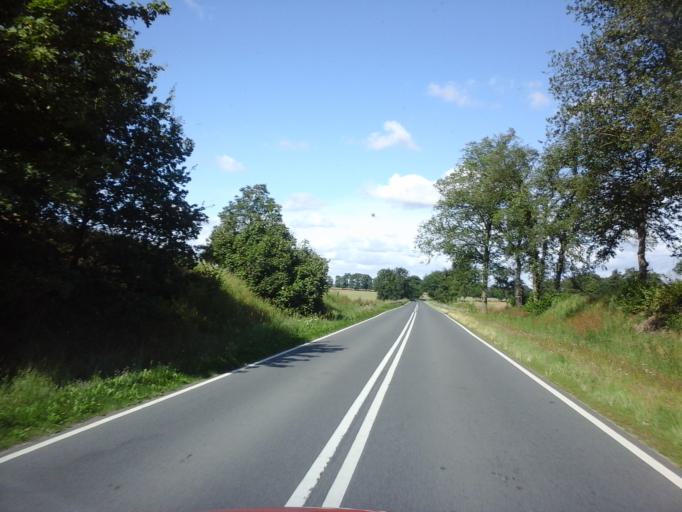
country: PL
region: West Pomeranian Voivodeship
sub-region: Powiat stargardzki
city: Dolice
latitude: 53.2021
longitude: 15.1582
